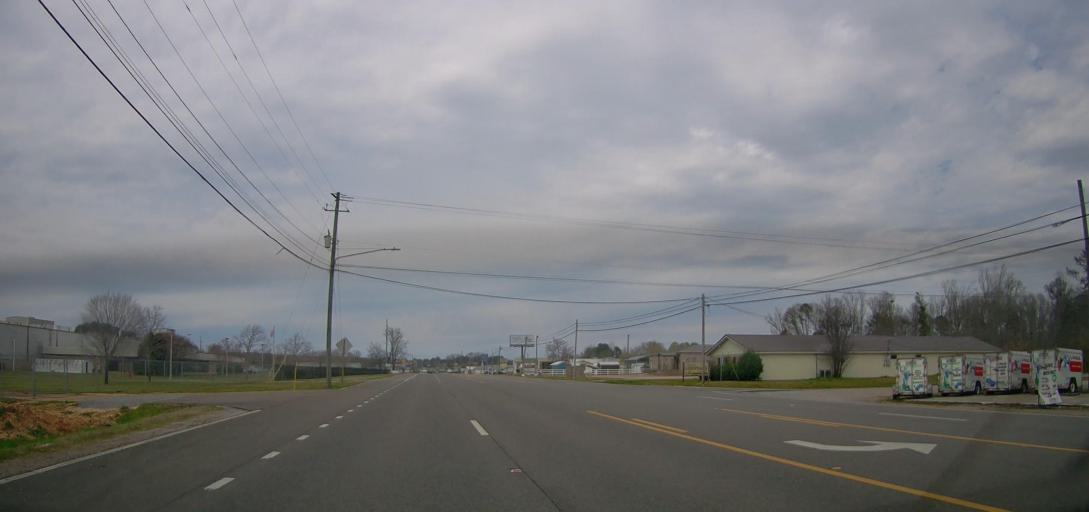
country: US
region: Alabama
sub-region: Marion County
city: Hamilton
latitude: 34.1124
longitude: -87.9894
